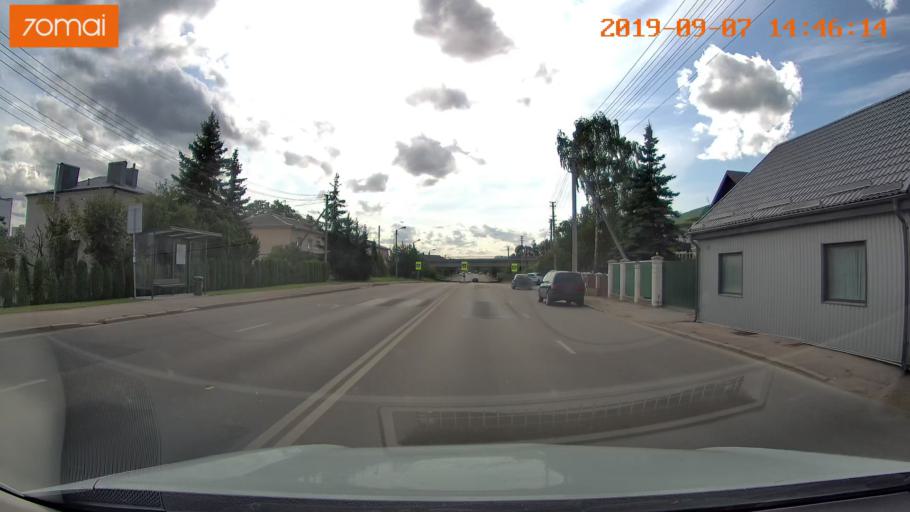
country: LT
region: Kauno apskritis
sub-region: Kaunas
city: Silainiai
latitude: 54.9271
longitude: 23.9054
